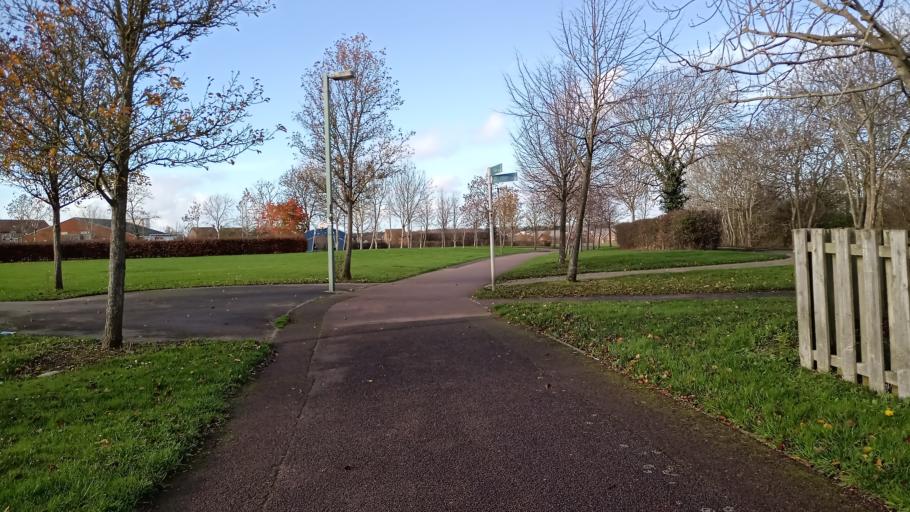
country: GB
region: England
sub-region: Milton Keynes
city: Shenley Church End
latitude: 52.0037
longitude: -0.7970
